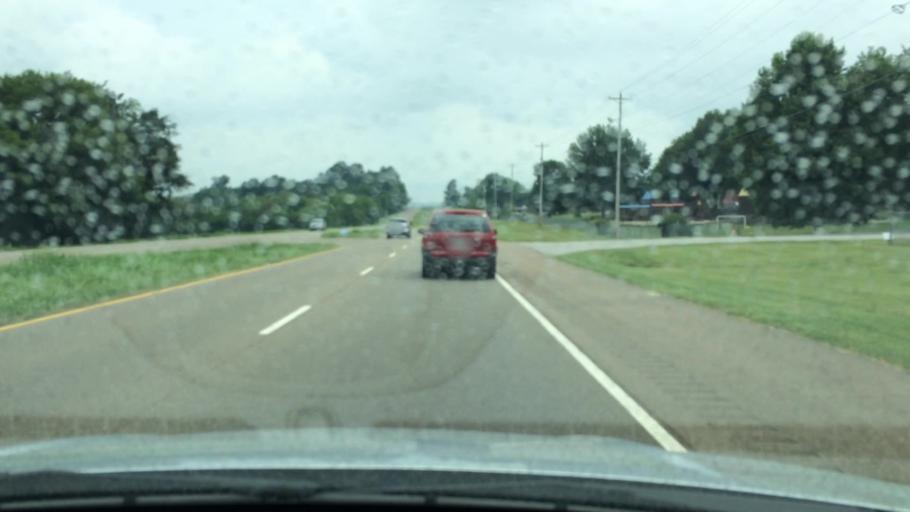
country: US
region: Tennessee
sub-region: Jefferson County
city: Jefferson City
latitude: 36.1105
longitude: -83.5120
